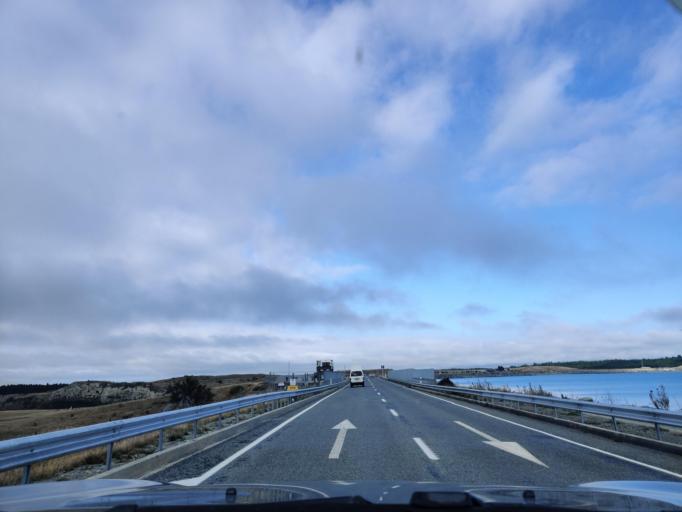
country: NZ
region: Canterbury
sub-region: Timaru District
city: Pleasant Point
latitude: -44.1874
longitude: 170.1504
